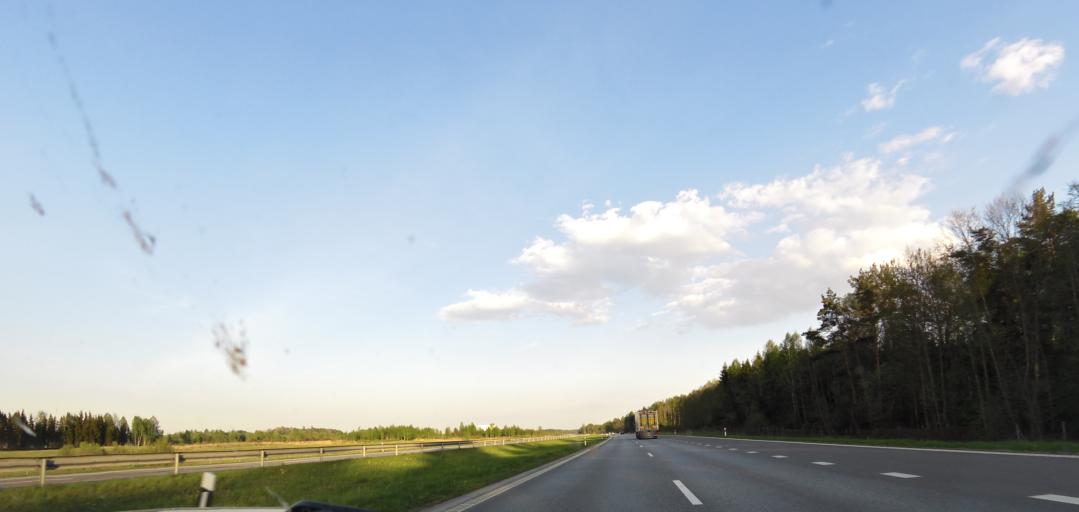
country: LT
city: Sirvintos
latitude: 54.9131
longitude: 25.0076
